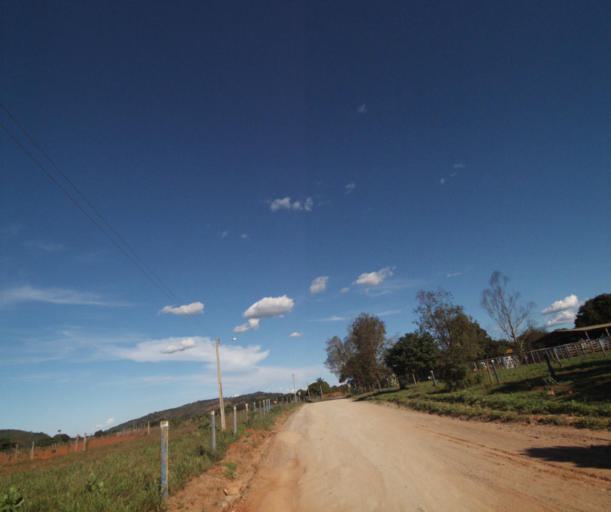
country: BR
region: Bahia
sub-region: Carinhanha
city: Carinhanha
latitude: -14.2818
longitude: -44.4911
